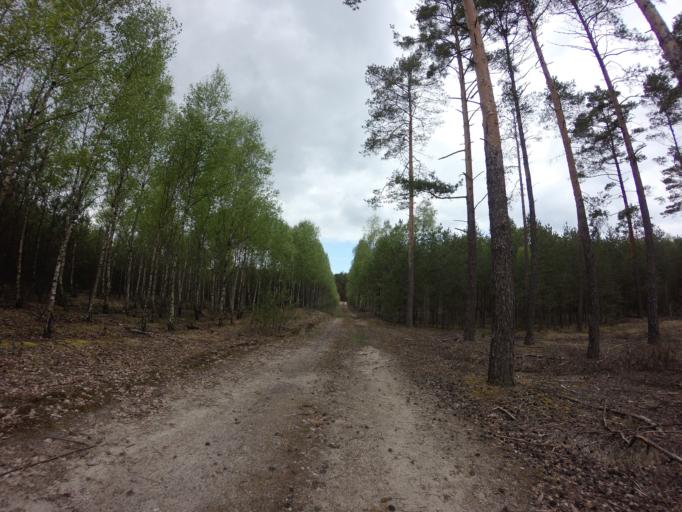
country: PL
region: West Pomeranian Voivodeship
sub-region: Powiat drawski
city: Kalisz Pomorski
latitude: 53.1908
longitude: 16.0008
